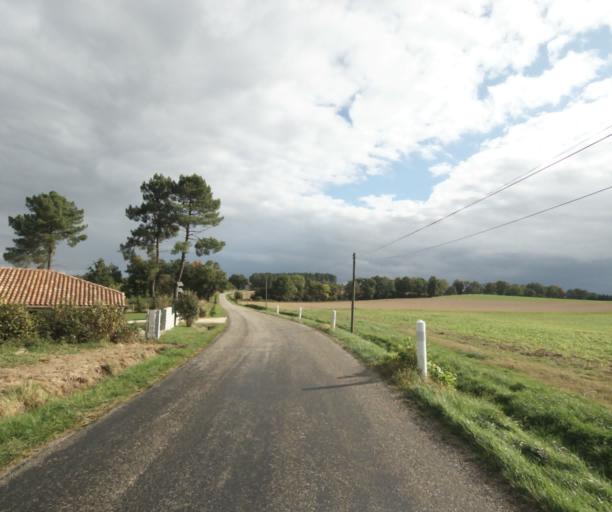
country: FR
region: Midi-Pyrenees
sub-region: Departement du Gers
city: Eauze
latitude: 43.9124
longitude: 0.0972
